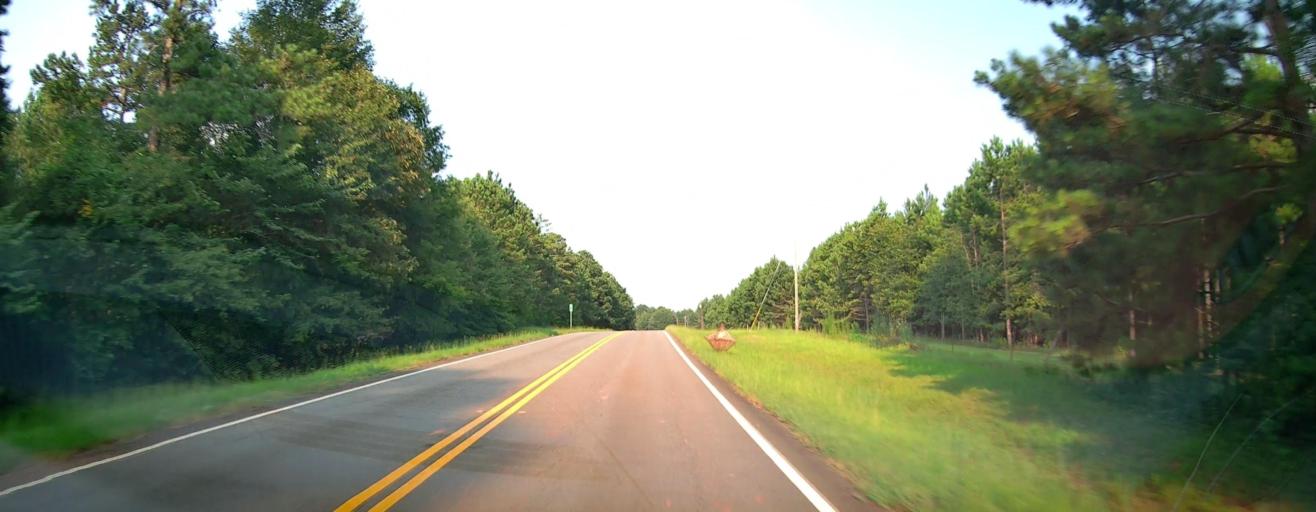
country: US
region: Georgia
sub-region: Jones County
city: Gray
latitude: 33.0599
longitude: -83.5946
